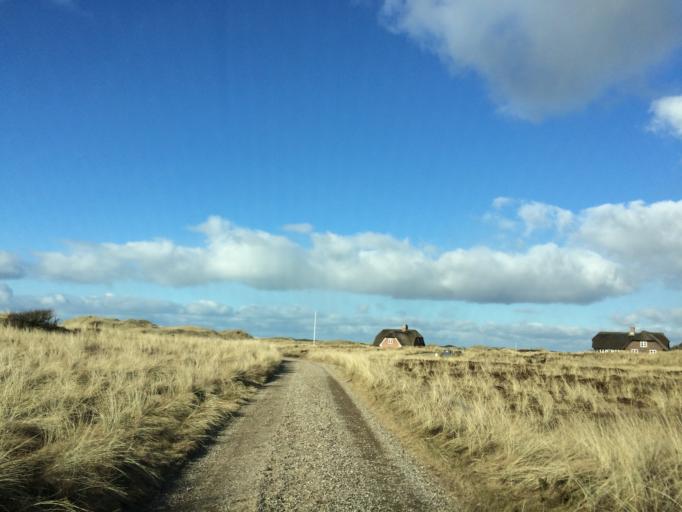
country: DK
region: Central Jutland
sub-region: Holstebro Kommune
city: Ulfborg
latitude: 56.2716
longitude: 8.1351
